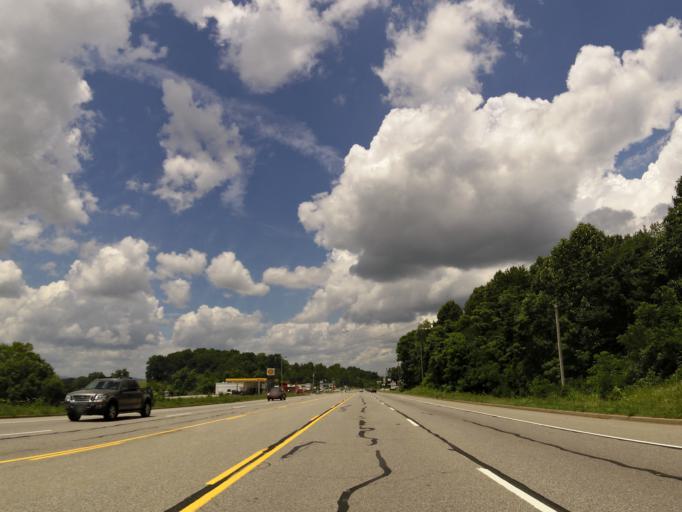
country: US
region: Tennessee
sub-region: Claiborne County
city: Tazewell
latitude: 36.4878
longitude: -83.5890
